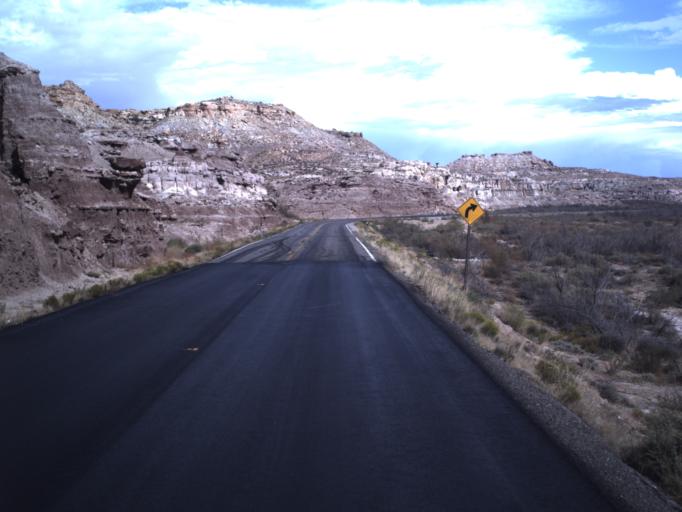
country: US
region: Utah
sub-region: San Juan County
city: Blanding
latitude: 37.2587
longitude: -109.2698
